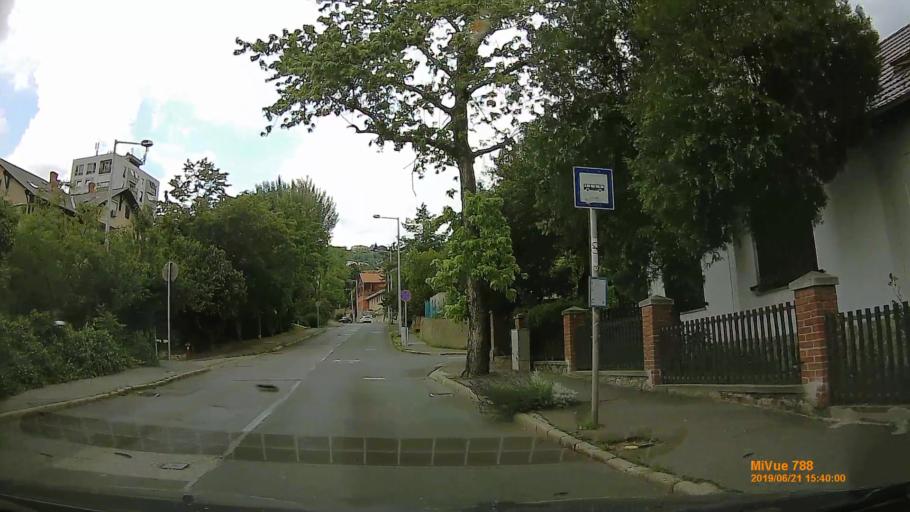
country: HU
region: Baranya
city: Pecs
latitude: 46.0815
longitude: 18.2158
